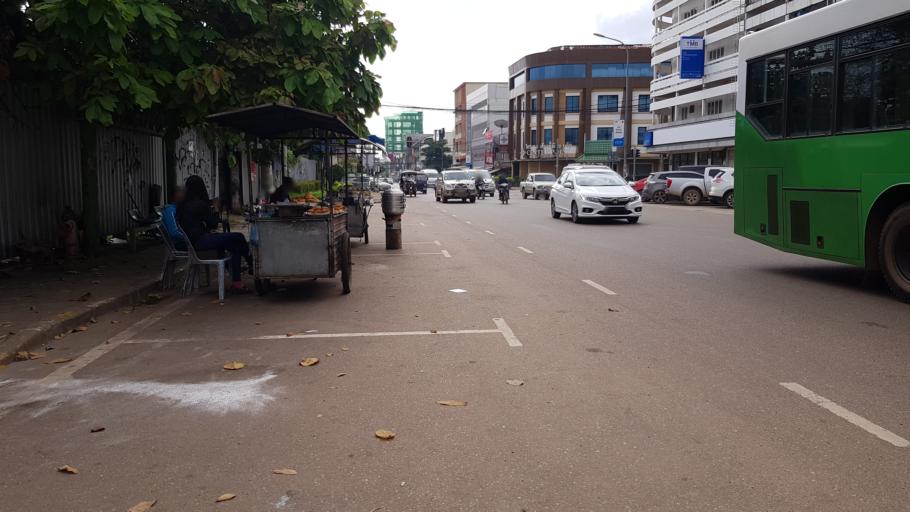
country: LA
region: Vientiane
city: Vientiane
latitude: 17.9691
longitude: 102.6027
